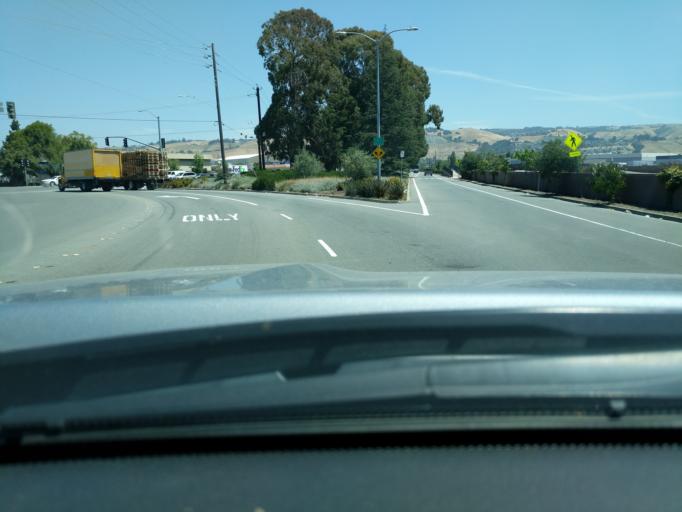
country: US
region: California
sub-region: Alameda County
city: Union City
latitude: 37.6175
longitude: -122.0621
